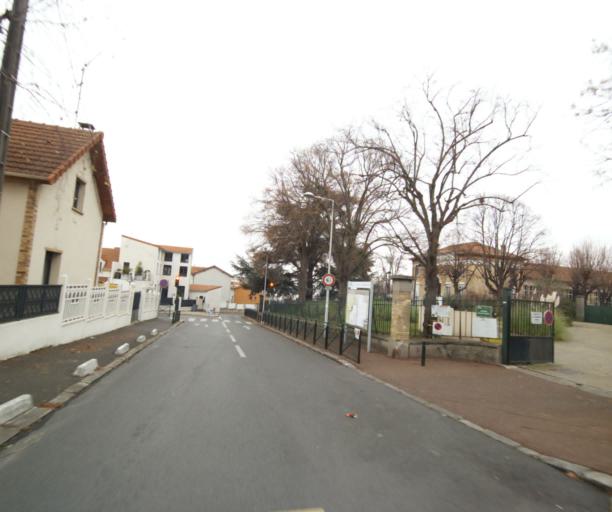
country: FR
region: Ile-de-France
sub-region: Departement des Hauts-de-Seine
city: Nanterre
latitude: 48.8824
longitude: 2.2015
